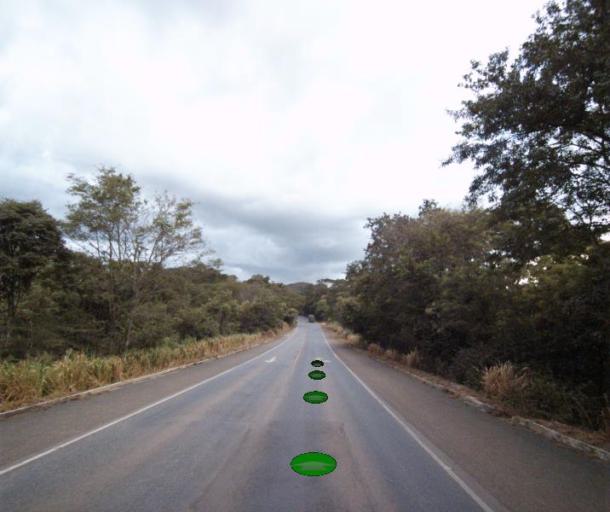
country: BR
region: Goias
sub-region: Uruacu
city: Uruacu
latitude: -14.7255
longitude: -49.2338
